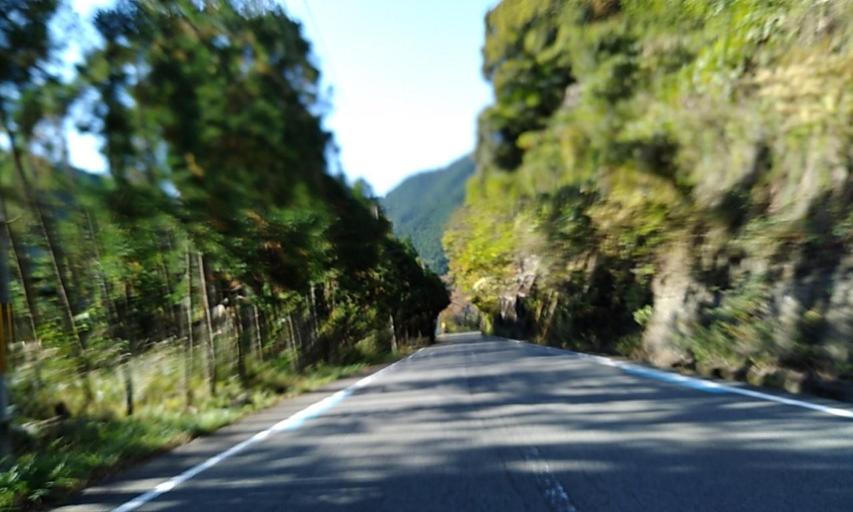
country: JP
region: Wakayama
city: Iwade
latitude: 34.0877
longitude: 135.3631
